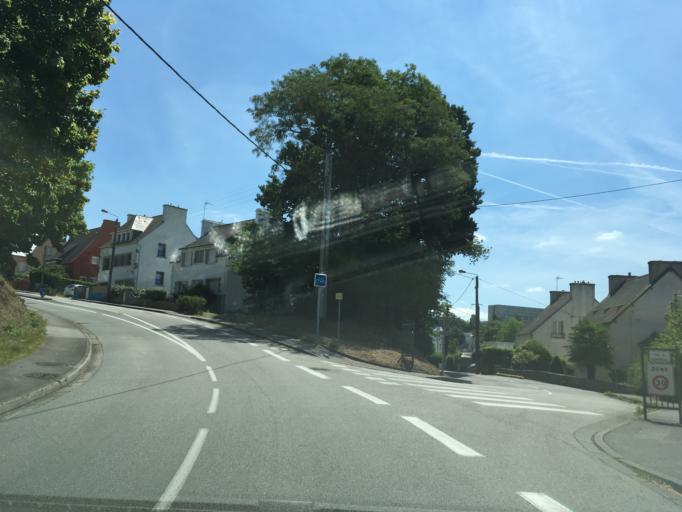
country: FR
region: Brittany
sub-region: Departement du Finistere
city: Quimper
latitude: 48.0052
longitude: -4.1055
